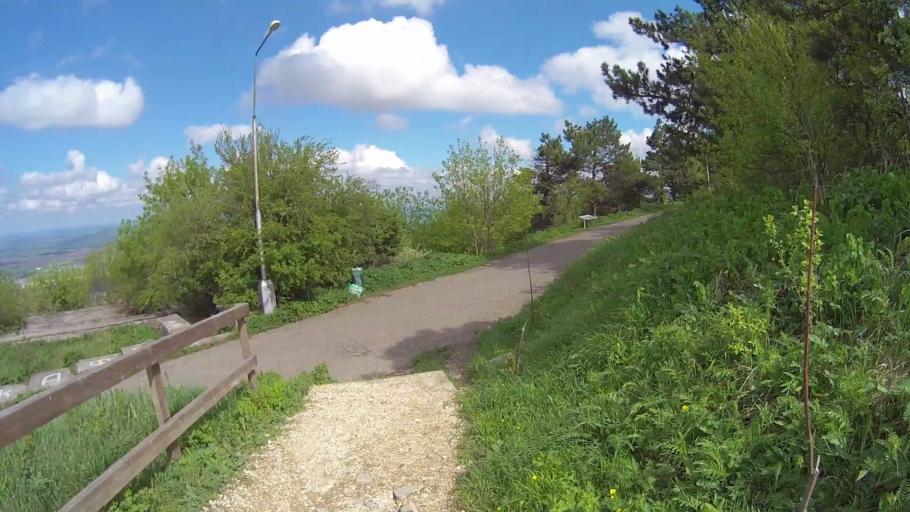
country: RU
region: Stavropol'skiy
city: Goryachevodskiy
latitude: 44.0507
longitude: 43.0887
